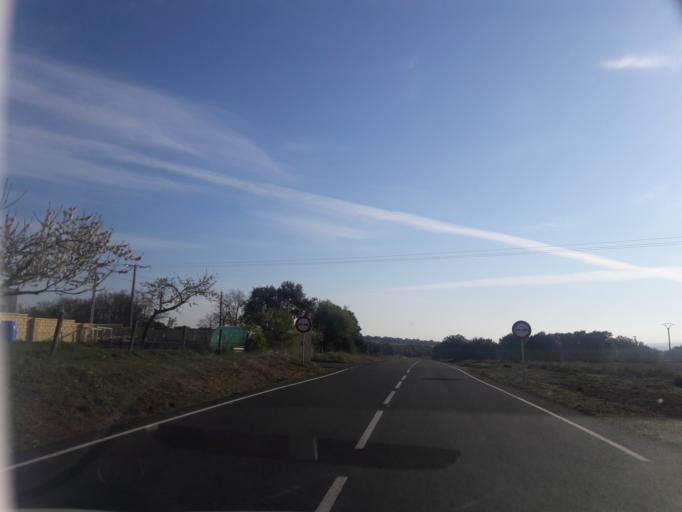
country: ES
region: Castille and Leon
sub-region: Provincia de Salamanca
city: Guijuelo
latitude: 40.5753
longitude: -5.6511
